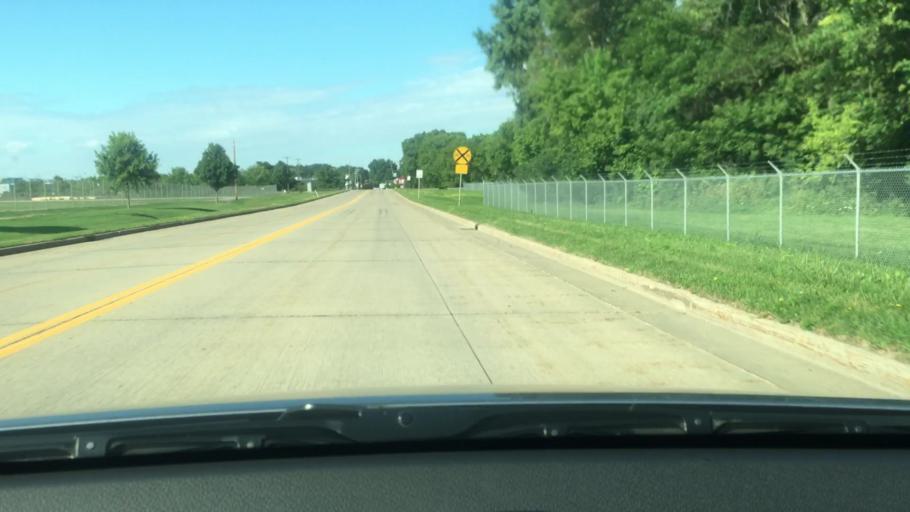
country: US
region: Wisconsin
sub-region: Winnebago County
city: Oshkosh
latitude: 43.9881
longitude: -88.5465
